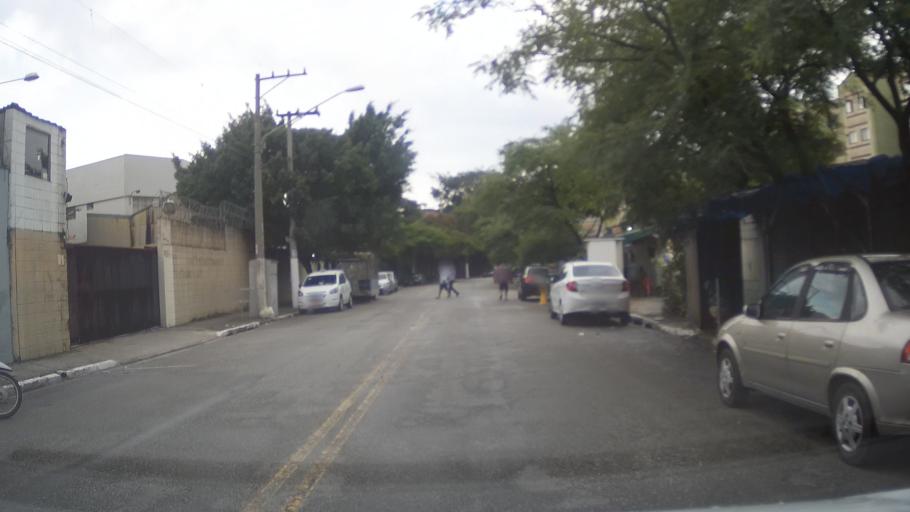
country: BR
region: Sao Paulo
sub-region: Sao Paulo
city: Sao Paulo
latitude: -23.5119
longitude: -46.6683
